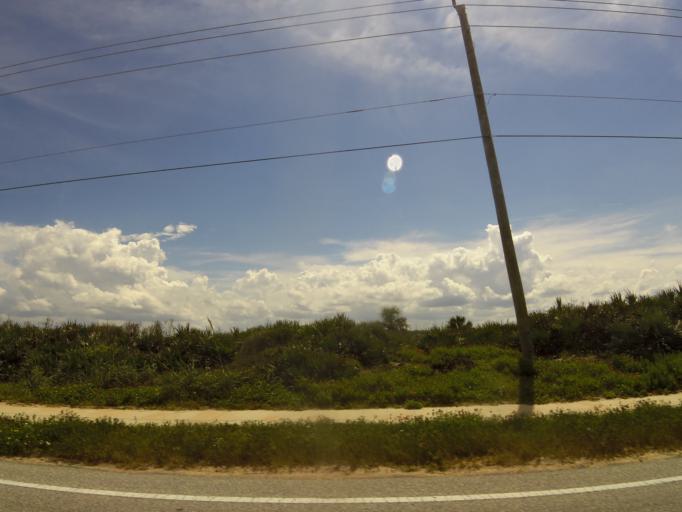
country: US
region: Florida
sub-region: Volusia County
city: Ormond-by-the-Sea
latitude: 29.4008
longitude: -81.0906
